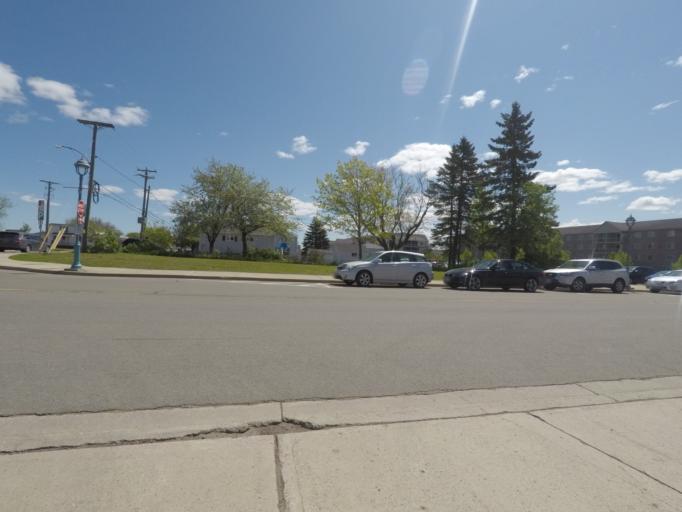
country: CA
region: New Brunswick
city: Moncton
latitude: 46.0944
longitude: -64.7460
